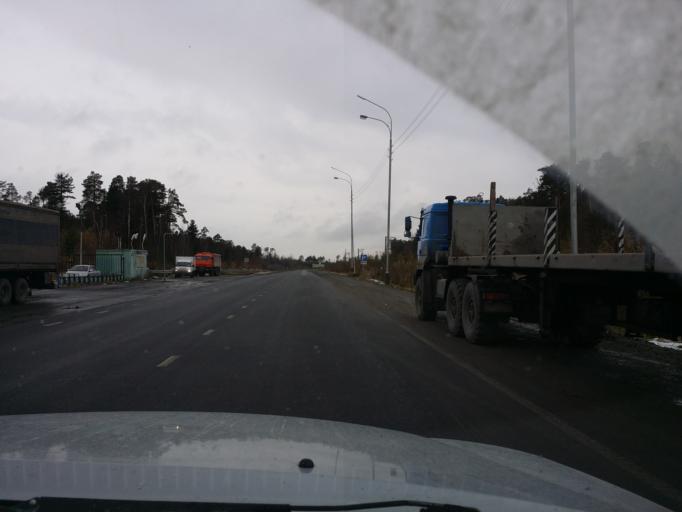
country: RU
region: Khanty-Mansiyskiy Avtonomnyy Okrug
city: Langepas
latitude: 61.2823
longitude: 75.1610
